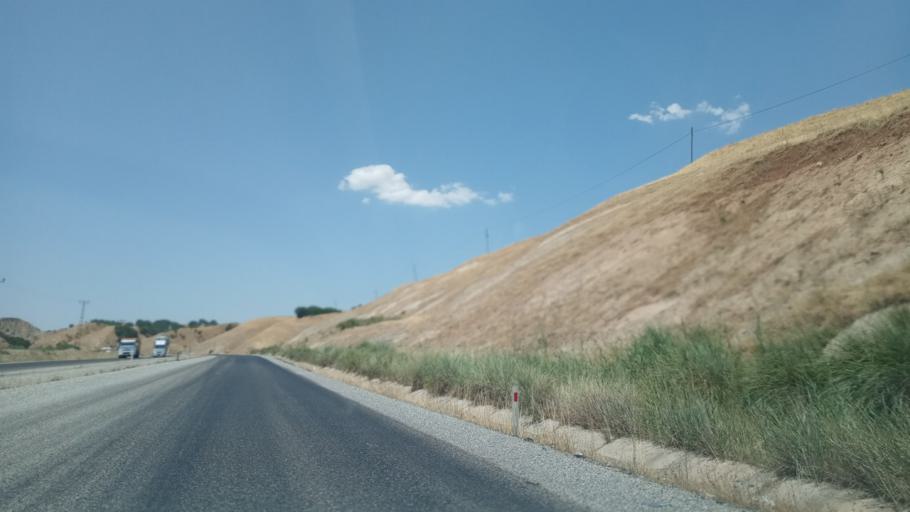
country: TR
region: Batman
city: Kozluk
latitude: 38.1686
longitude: 41.4668
